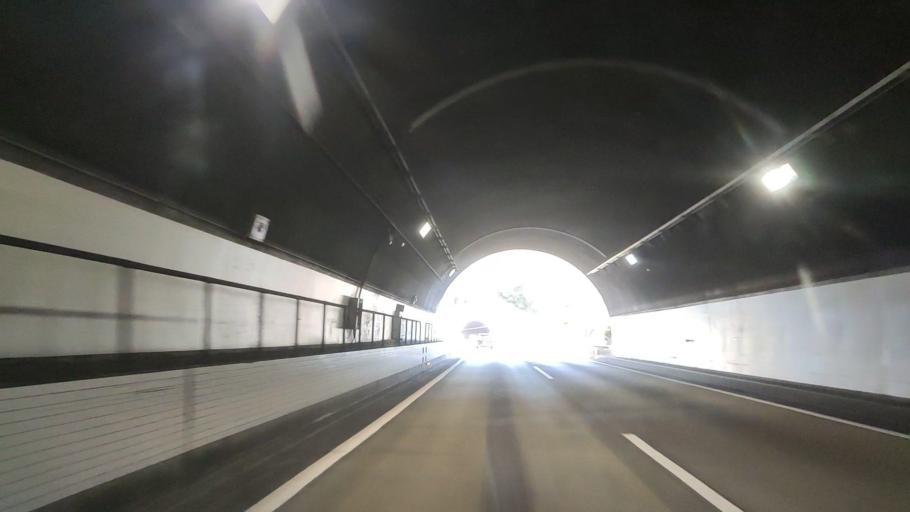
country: JP
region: Hiroshima
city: Fukuyama
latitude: 34.4760
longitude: 133.2887
